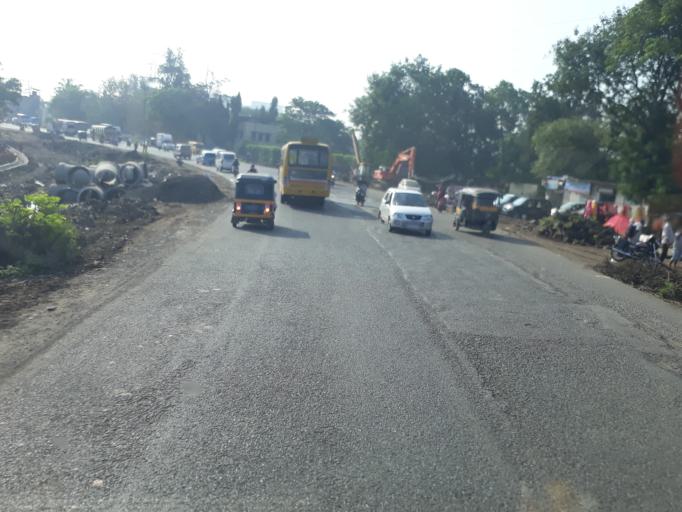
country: IN
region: Maharashtra
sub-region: Raigarh
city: Kalundri
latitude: 18.9760
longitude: 73.1174
